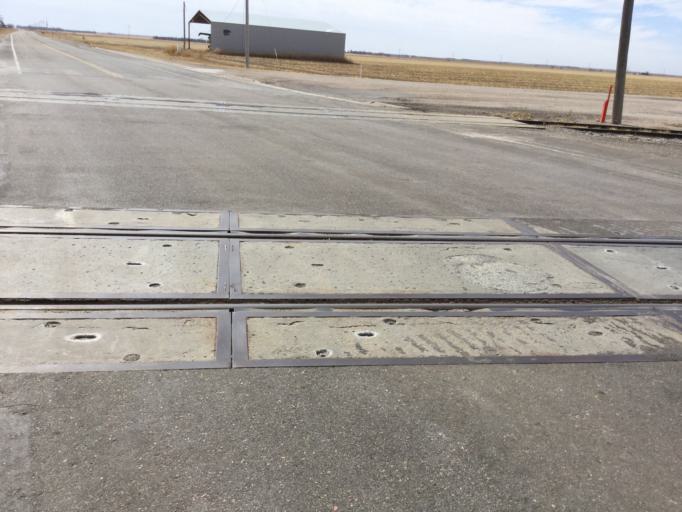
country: US
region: Kansas
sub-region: Pawnee County
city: Larned
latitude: 38.1810
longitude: -99.3142
